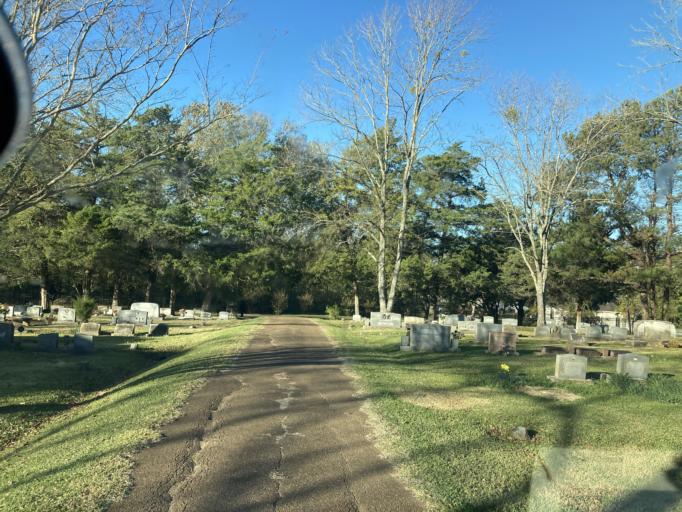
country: US
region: Mississippi
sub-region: Yazoo County
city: Yazoo City
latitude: 32.8517
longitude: -90.4016
